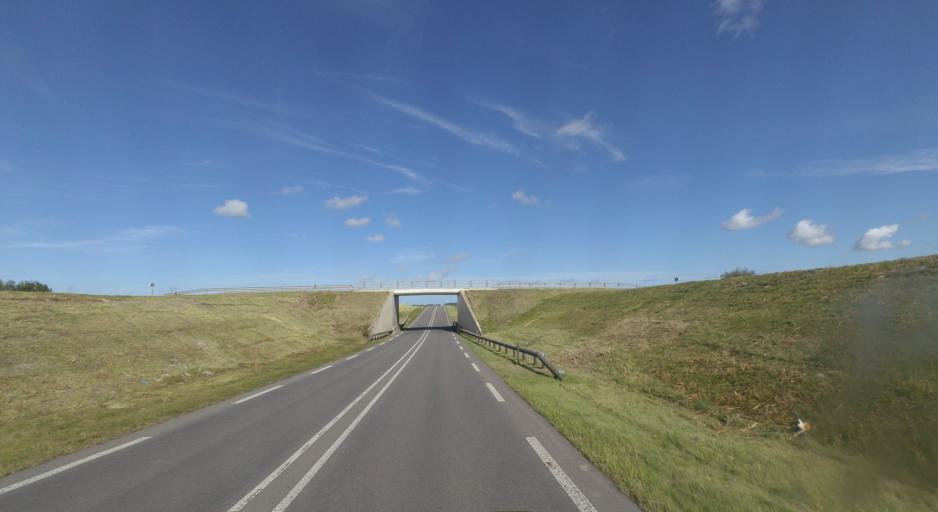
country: NL
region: Friesland
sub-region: Gemeente Leeuwarderadeel
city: Stiens
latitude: 53.2473
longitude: 5.7243
